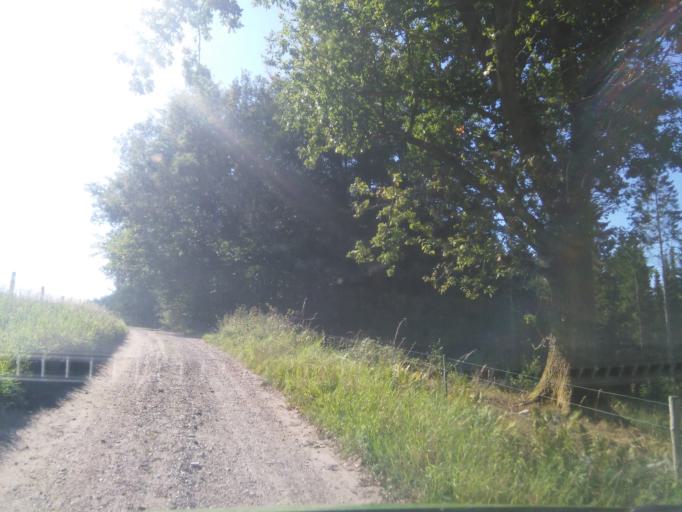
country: DK
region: Central Jutland
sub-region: Syddjurs Kommune
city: Ronde
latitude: 56.2091
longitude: 10.5240
